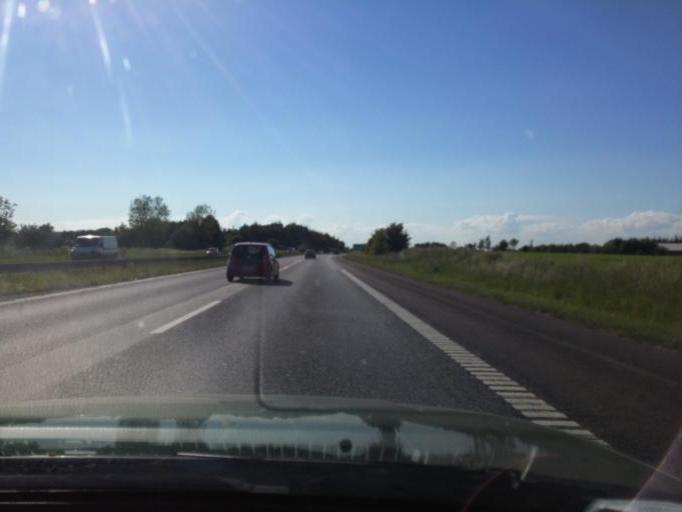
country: DK
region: South Denmark
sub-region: Middelfart Kommune
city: Norre Aby
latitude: 55.4636
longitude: 9.9108
